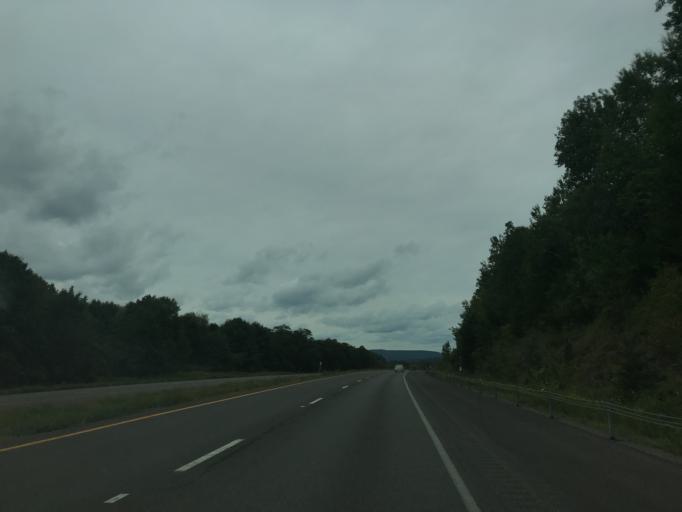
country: US
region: New York
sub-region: Otsego County
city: Unadilla
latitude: 42.3175
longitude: -75.3165
